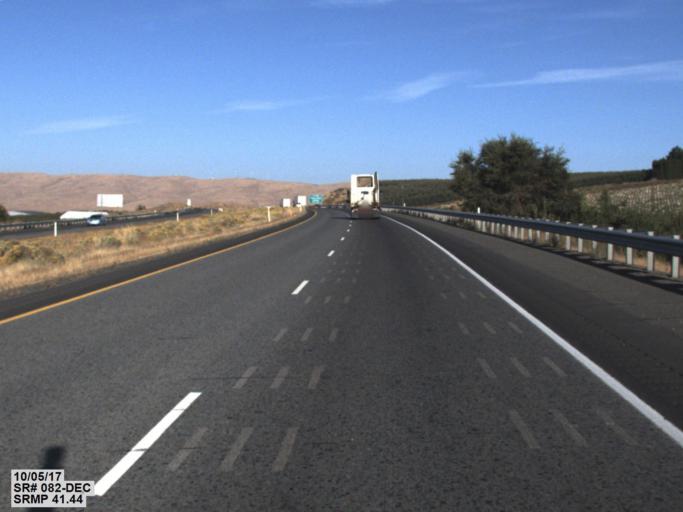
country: US
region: Washington
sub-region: Yakima County
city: Wapato
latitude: 46.4984
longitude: -120.4404
